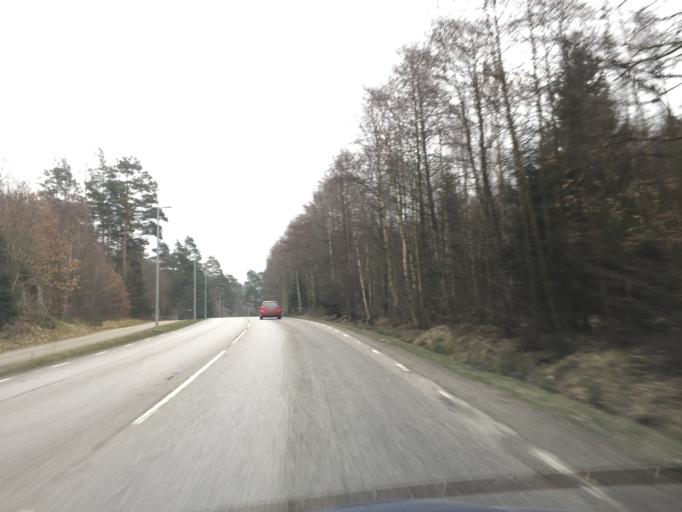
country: SE
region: Vaestra Goetaland
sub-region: Goteborg
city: Rannebergen
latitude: 57.7704
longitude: 12.0740
